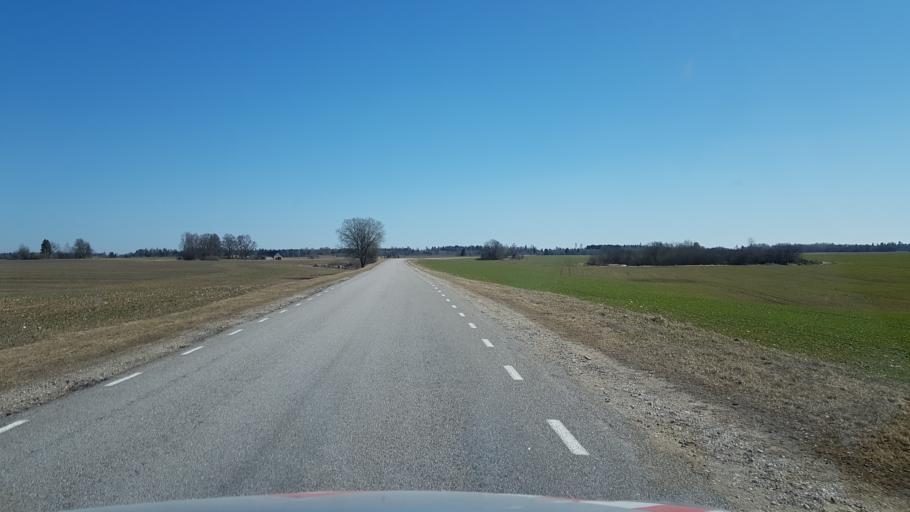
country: EE
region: Laeaene-Virumaa
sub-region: Vaeike-Maarja vald
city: Vaike-Maarja
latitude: 59.1078
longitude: 26.3799
